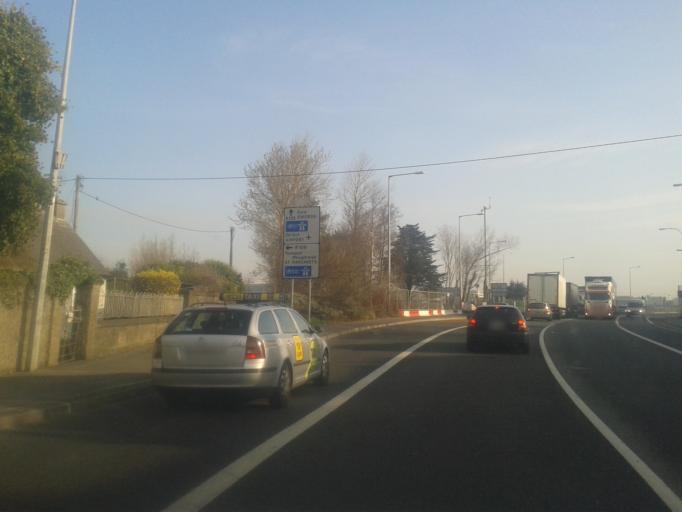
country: IE
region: Leinster
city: Beaumont
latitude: 53.4163
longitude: -6.2393
